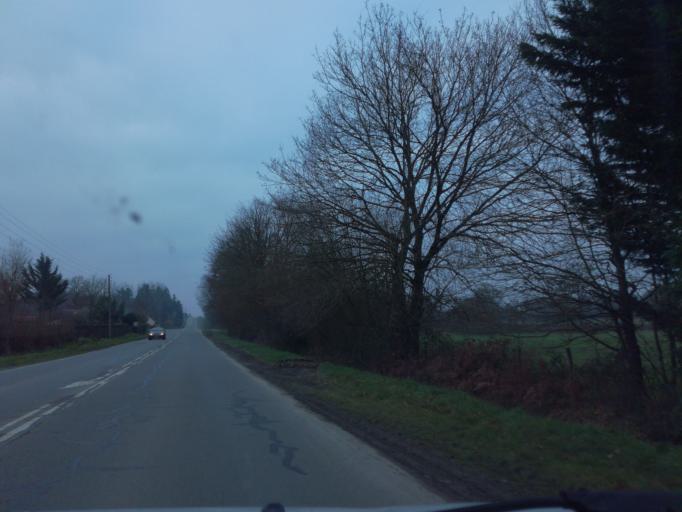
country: FR
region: Brittany
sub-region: Departement d'Ille-et-Vilaine
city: Gosne
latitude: 48.2266
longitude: -1.4827
